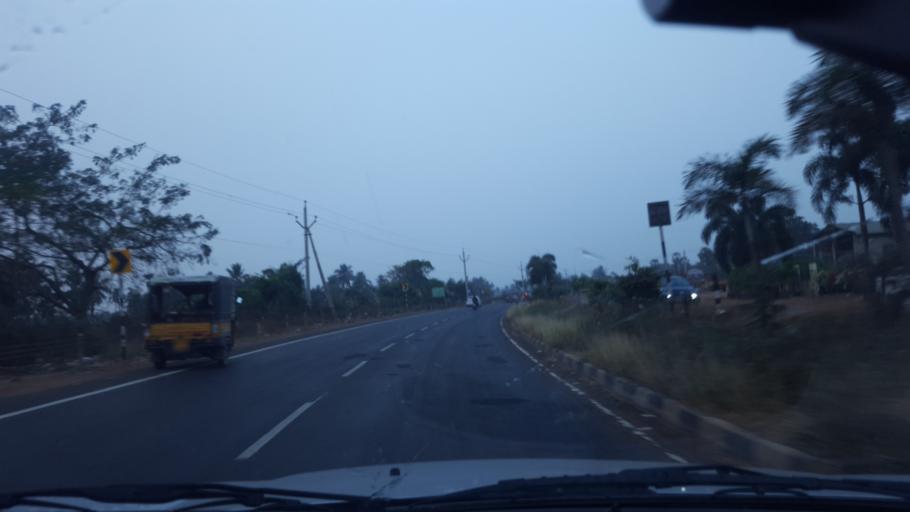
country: IN
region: Andhra Pradesh
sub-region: East Godavari
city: Mandapeta
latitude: 16.8806
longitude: 81.8082
